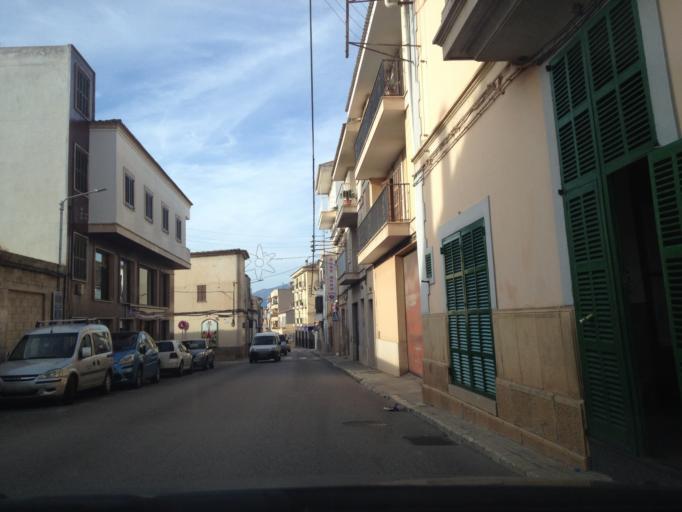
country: ES
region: Balearic Islands
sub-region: Illes Balears
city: Muro
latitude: 39.7372
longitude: 3.0554
